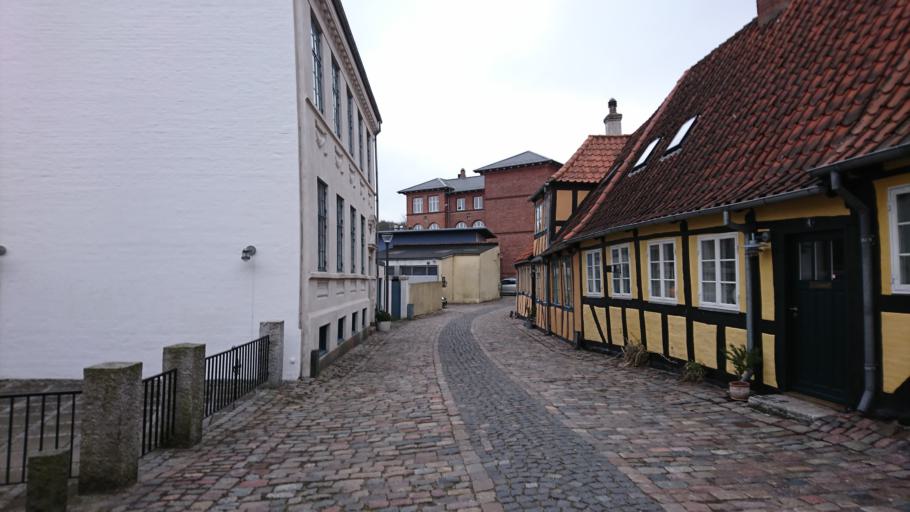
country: DK
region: South Denmark
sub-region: Svendborg Kommune
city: Svendborg
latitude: 55.0584
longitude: 10.6096
